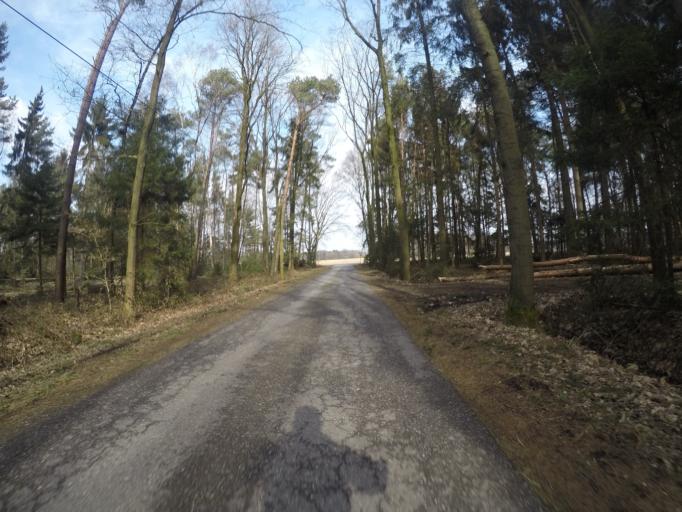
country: DE
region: North Rhine-Westphalia
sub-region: Regierungsbezirk Munster
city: Rhede
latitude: 51.7835
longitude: 6.7276
